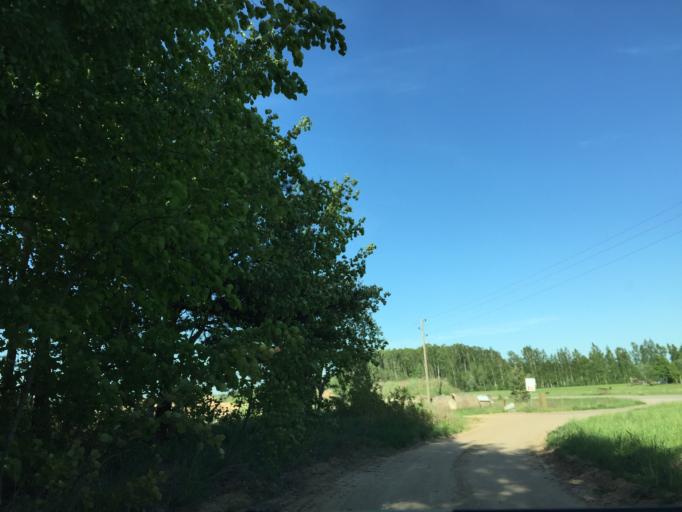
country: LV
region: Jelgava
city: Jelgava
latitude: 56.5470
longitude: 23.6266
